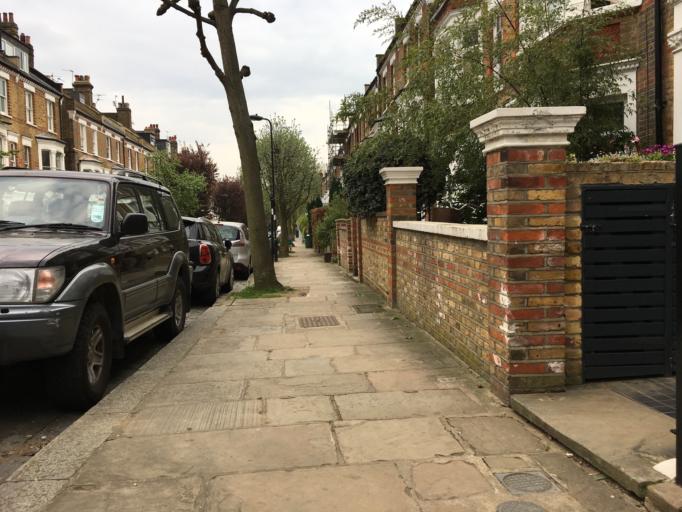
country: GB
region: England
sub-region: Greater London
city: Camden Town
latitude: 51.5548
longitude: -0.1550
